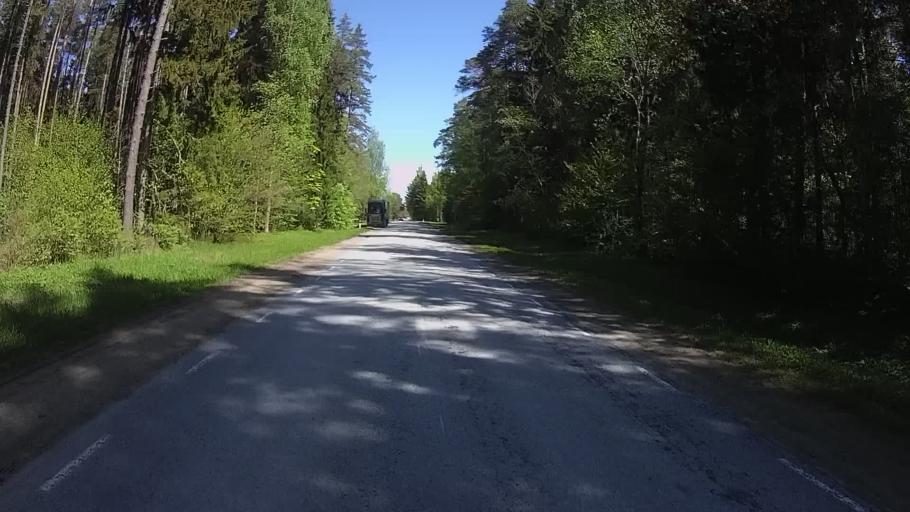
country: EE
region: Polvamaa
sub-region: Raepina vald
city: Rapina
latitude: 58.0818
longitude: 27.4326
